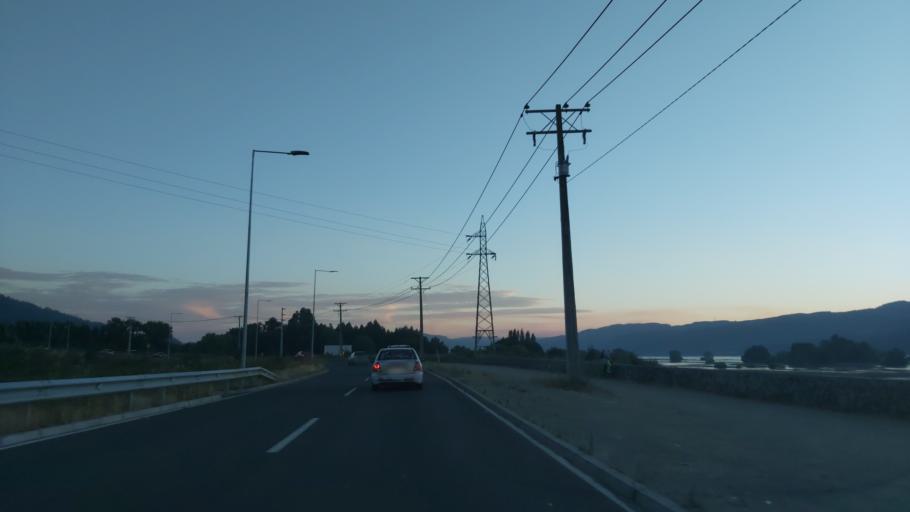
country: CL
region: Biobio
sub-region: Provincia de Concepcion
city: Chiguayante
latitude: -36.8931
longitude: -73.0366
